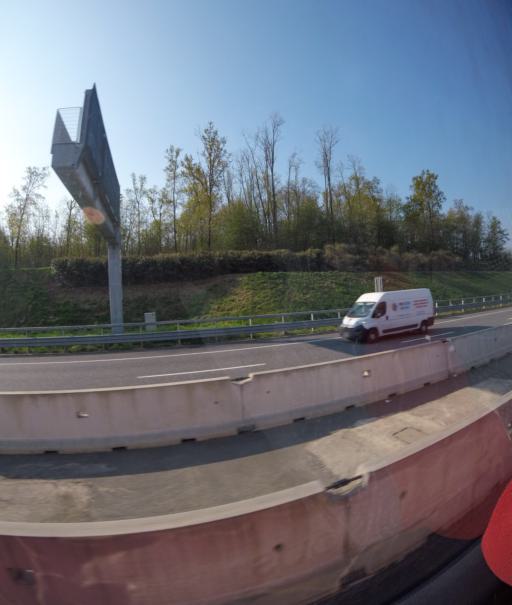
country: IT
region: Lombardy
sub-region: Provincia di Varese
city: Gorla Maggiore
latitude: 45.6583
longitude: 8.9102
